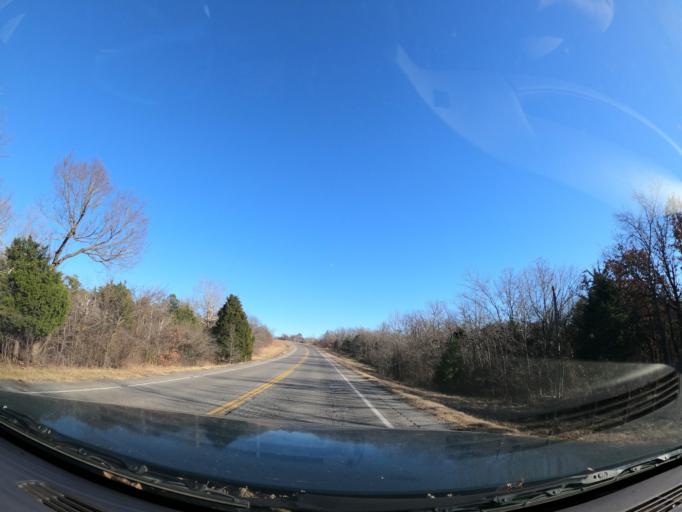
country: US
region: Oklahoma
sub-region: Pittsburg County
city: Longtown
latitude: 35.2259
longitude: -95.4460
